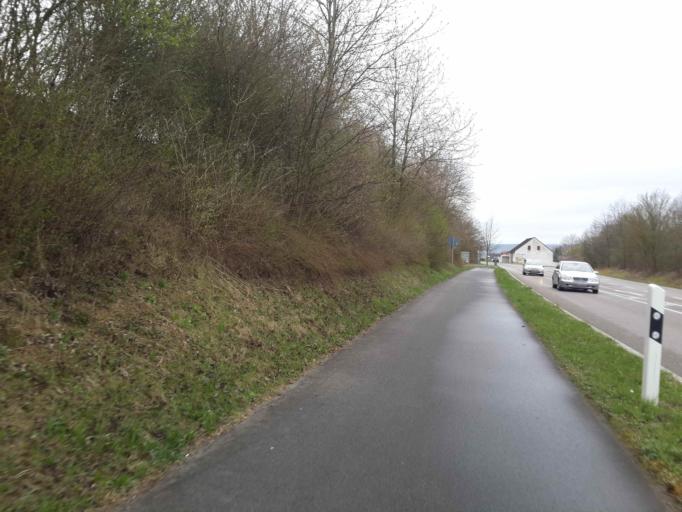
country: DE
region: Baden-Wuerttemberg
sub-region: Regierungsbezirk Stuttgart
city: Lauda-Konigshofen
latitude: 49.5314
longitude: 9.7427
